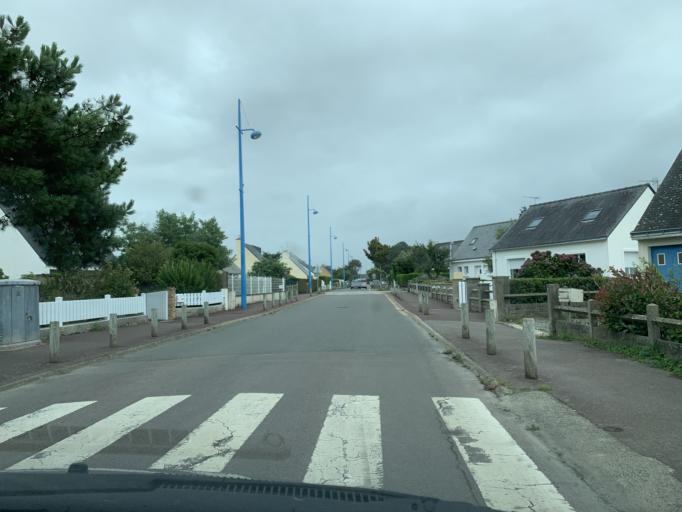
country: FR
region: Brittany
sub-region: Departement du Morbihan
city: Penestin
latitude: 47.4748
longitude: -2.4844
